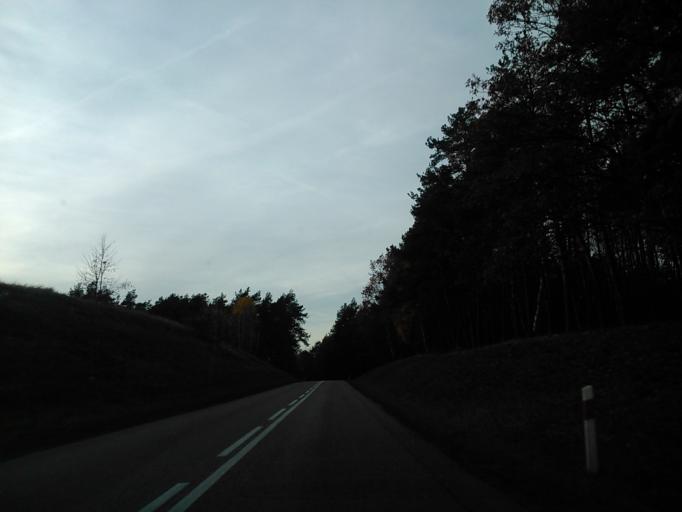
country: PL
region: Warmian-Masurian Voivodeship
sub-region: Powiat dzialdowski
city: Lidzbark
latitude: 53.2699
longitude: 19.8130
